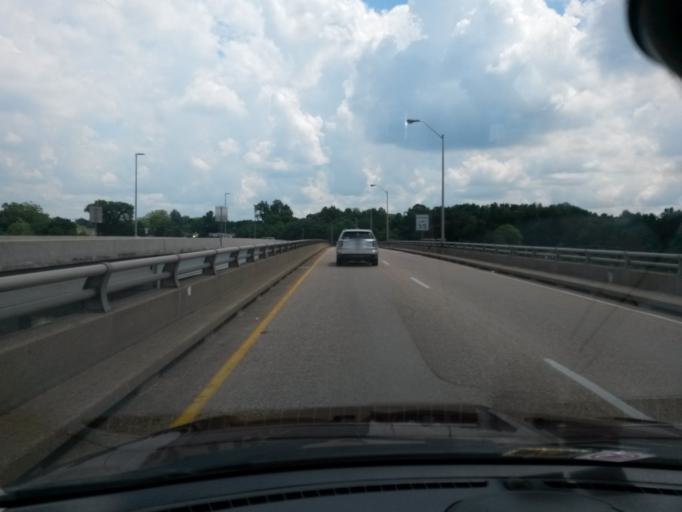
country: US
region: Virginia
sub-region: City of Hopewell
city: Hopewell
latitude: 37.3123
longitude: -77.2970
